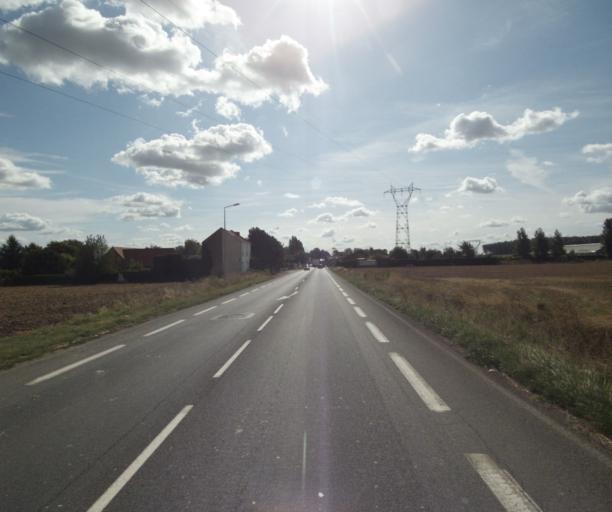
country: FR
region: Nord-Pas-de-Calais
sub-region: Departement du Nord
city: Sainghin-en-Melantois
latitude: 50.5905
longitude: 3.1550
